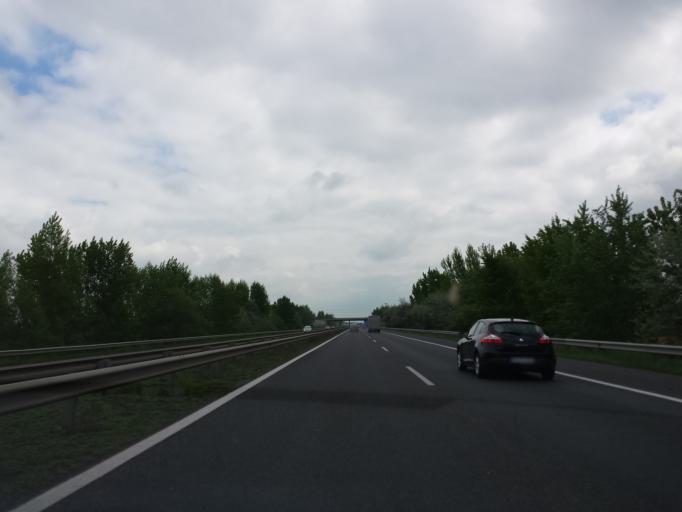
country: HU
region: Gyor-Moson-Sopron
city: Gyorujbarat
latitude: 47.6412
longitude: 17.6339
